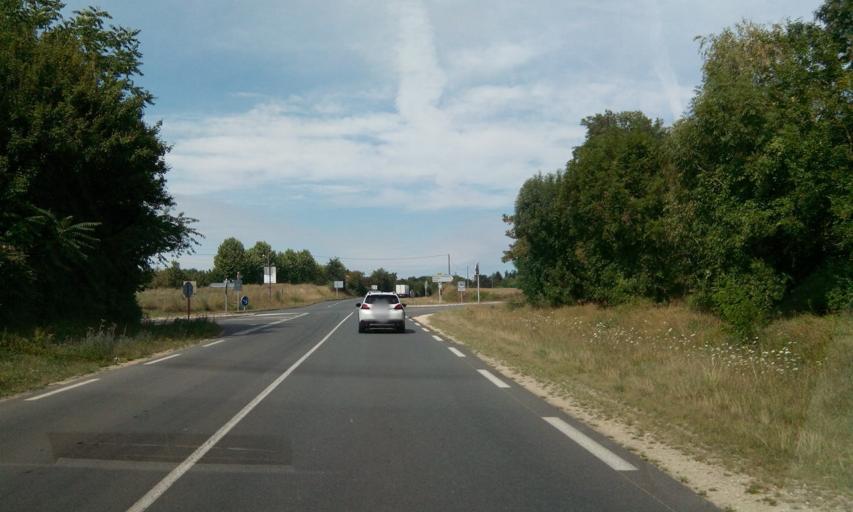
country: FR
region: Poitou-Charentes
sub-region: Departement des Deux-Sevres
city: Sauze-Vaussais
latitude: 46.1385
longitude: 0.1012
